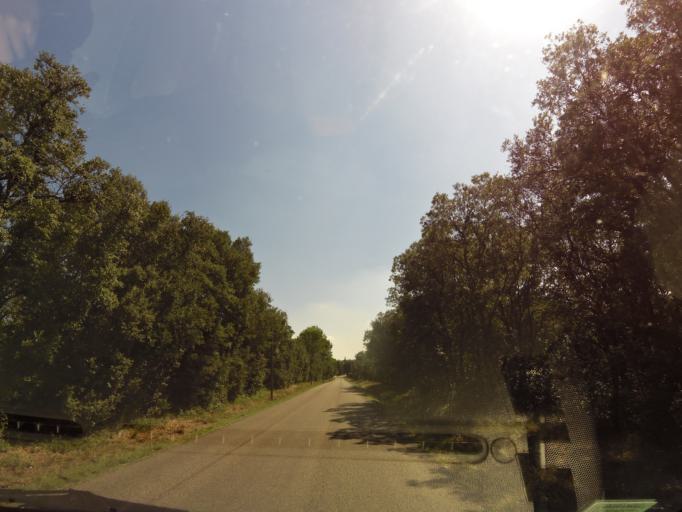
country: FR
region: Languedoc-Roussillon
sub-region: Departement du Gard
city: Villevieille
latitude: 43.8038
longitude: 4.1033
